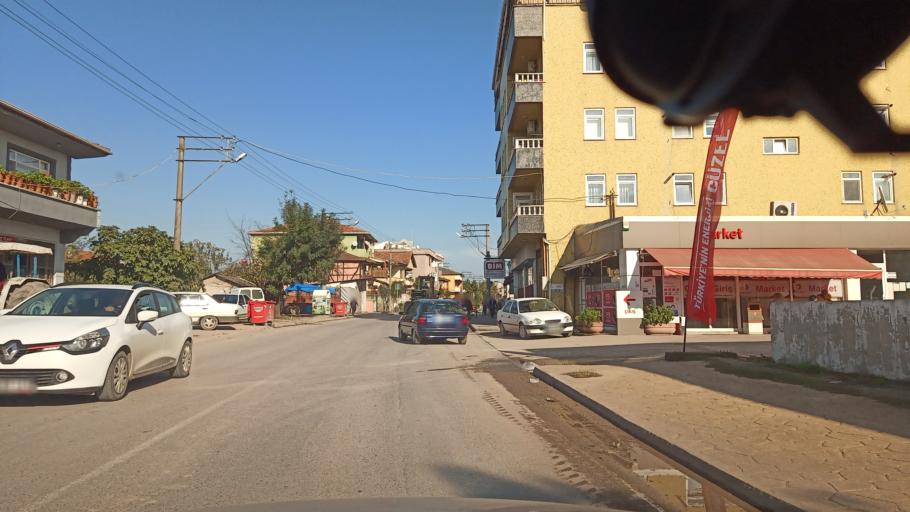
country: TR
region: Sakarya
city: Sogutlu
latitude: 40.9035
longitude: 30.4712
